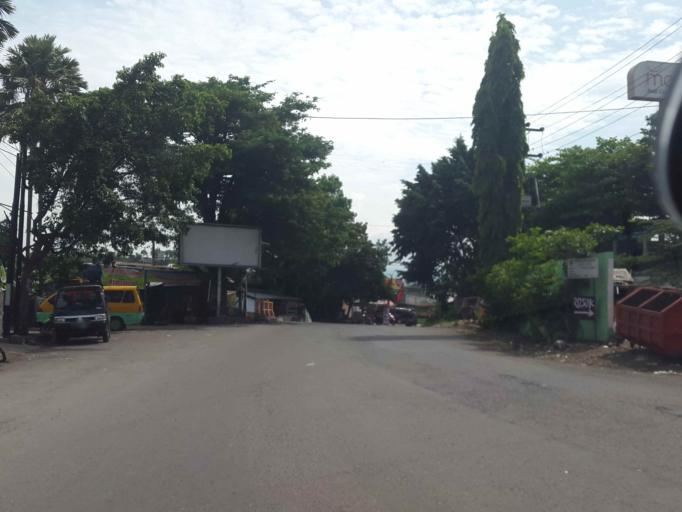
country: ID
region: Central Java
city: Semarang
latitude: -6.9931
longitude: 110.3680
